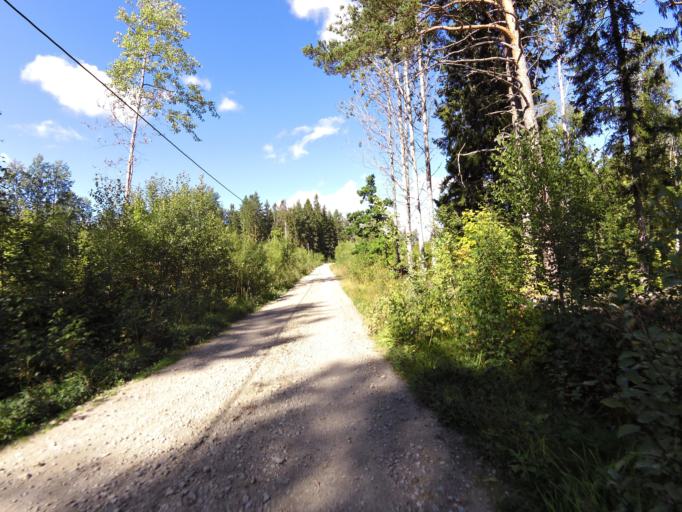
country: SE
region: Gaevleborg
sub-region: Gavle Kommun
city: Valbo
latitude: 60.7663
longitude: 16.9655
